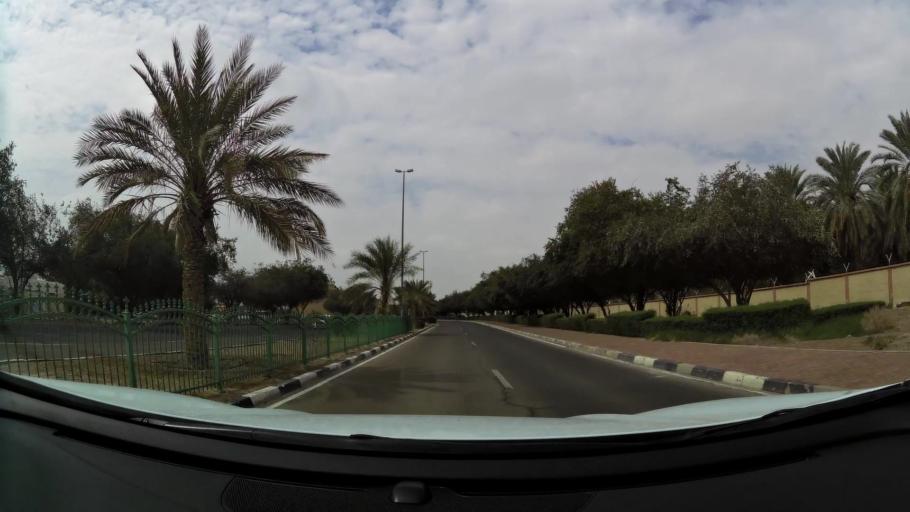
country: OM
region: Al Buraimi
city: Al Buraymi
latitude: 24.2147
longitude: 55.7902
